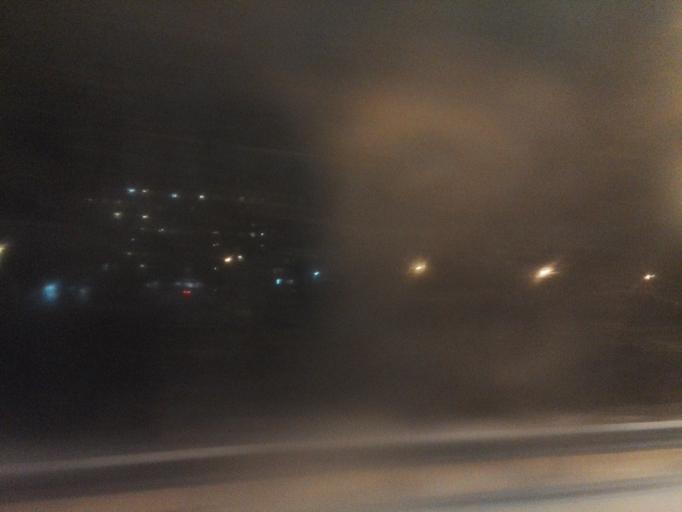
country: RU
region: Tula
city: Tula
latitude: 54.1727
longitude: 37.6382
